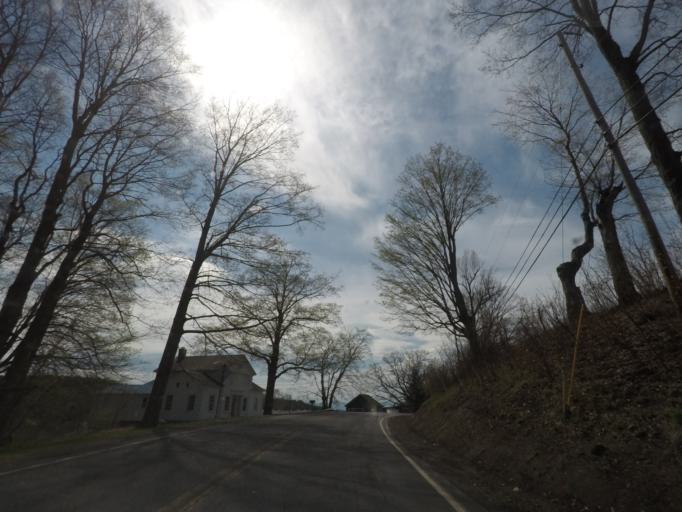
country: US
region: New York
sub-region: Columbia County
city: Chatham
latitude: 42.3563
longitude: -73.5396
